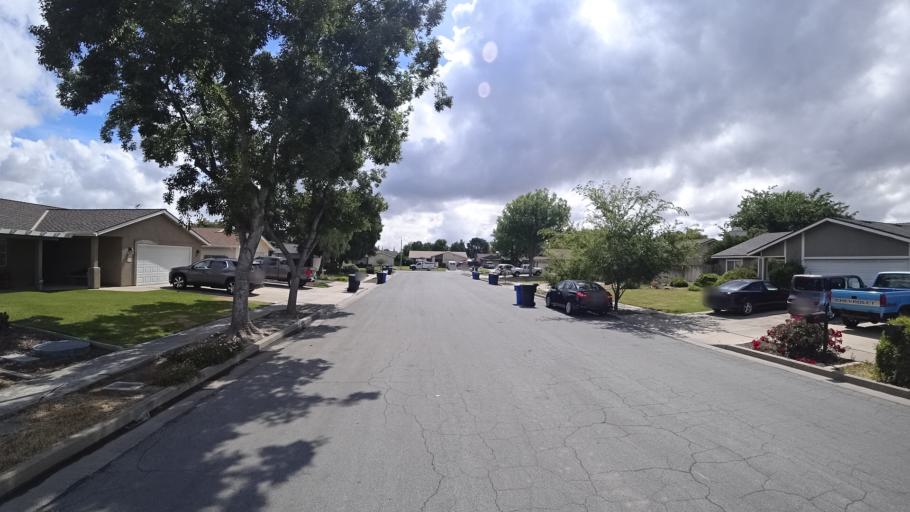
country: US
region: California
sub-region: Kings County
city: Hanford
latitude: 36.3403
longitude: -119.6667
